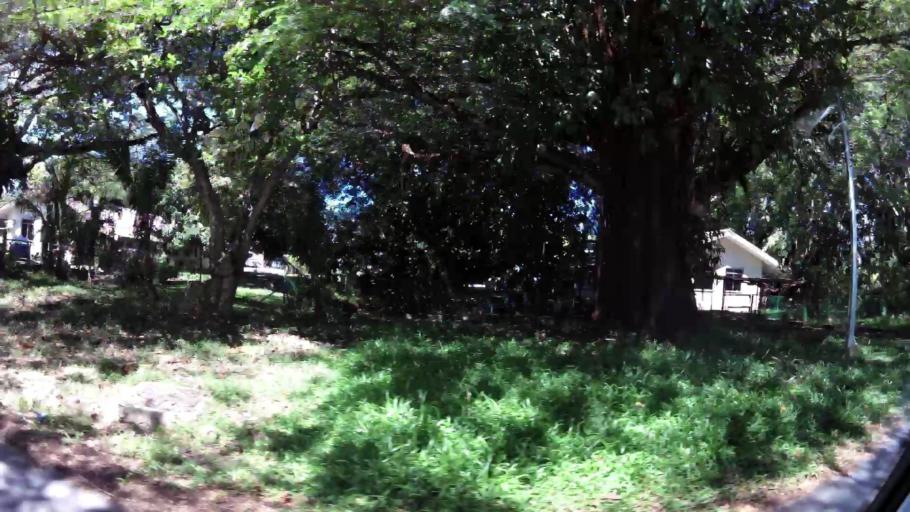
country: BN
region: Brunei and Muara
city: Bandar Seri Begawan
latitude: 5.0336
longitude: 115.0707
